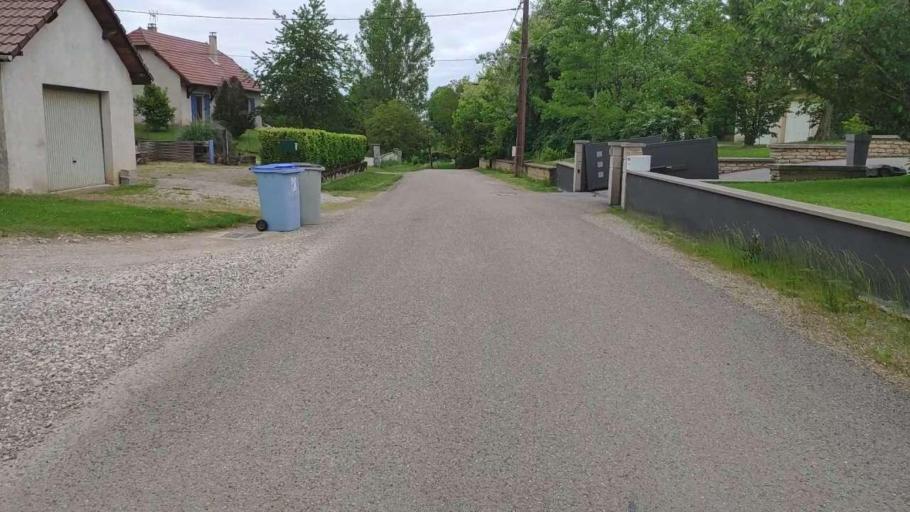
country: FR
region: Franche-Comte
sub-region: Departement du Jura
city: Montmorot
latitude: 46.7521
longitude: 5.5624
